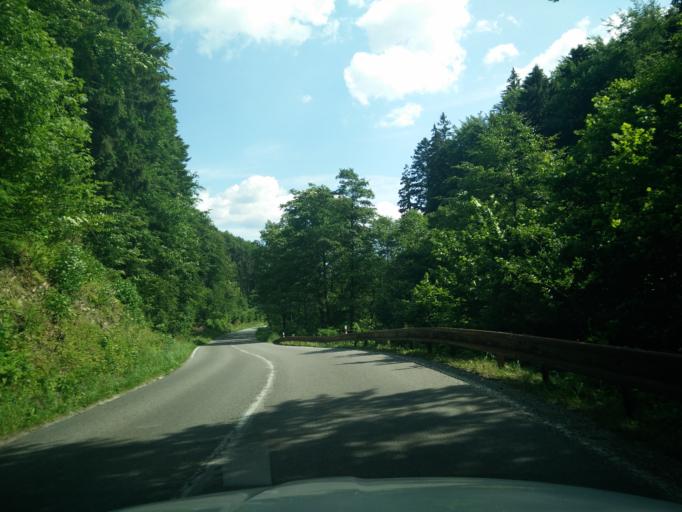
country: SK
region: Zilinsky
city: Rajec
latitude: 48.9425
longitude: 18.6282
